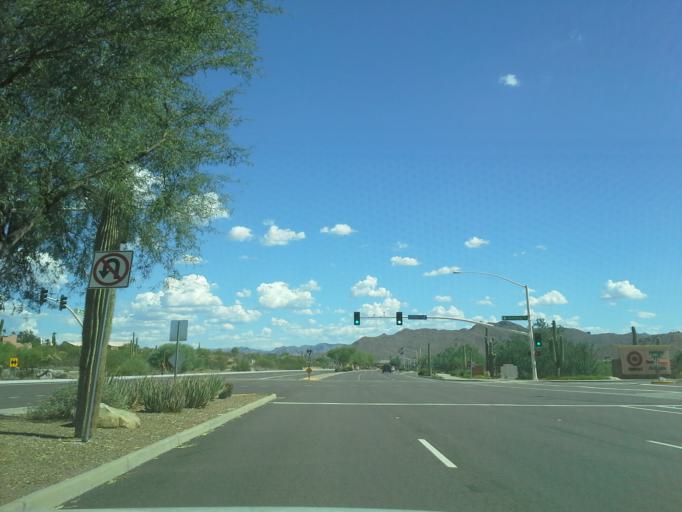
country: US
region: Arizona
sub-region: Maricopa County
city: Fountain Hills
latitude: 33.5765
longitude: -111.7205
